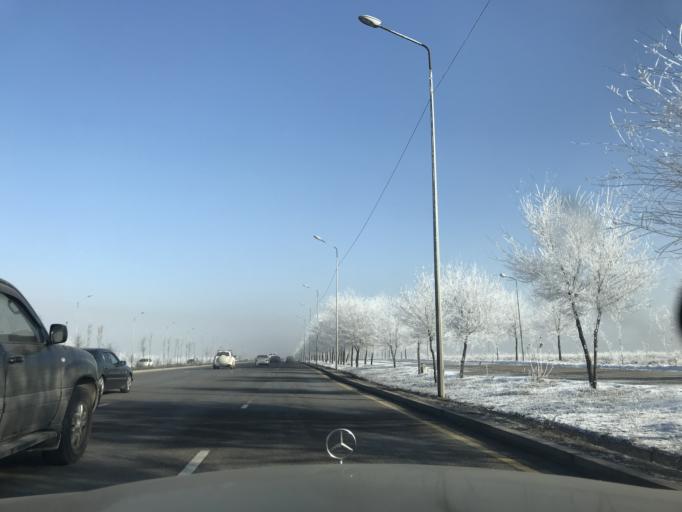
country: KZ
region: Almaty Oblysy
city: Burunday
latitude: 43.2906
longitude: 76.8287
